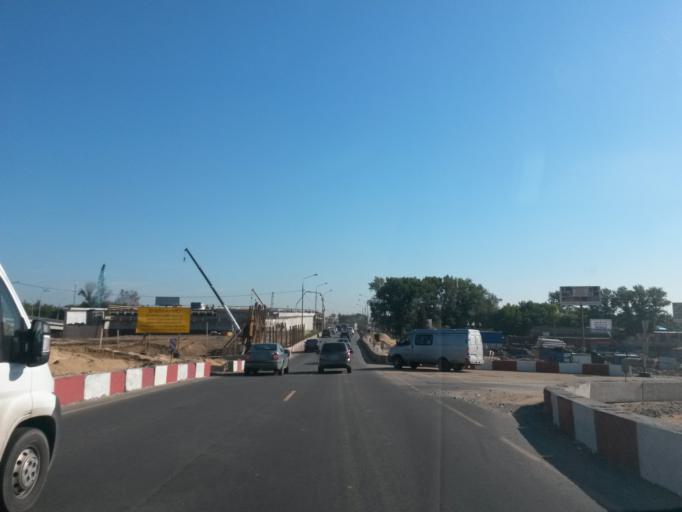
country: RU
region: Moskovskaya
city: Mamontovka
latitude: 55.9624
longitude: 37.8375
